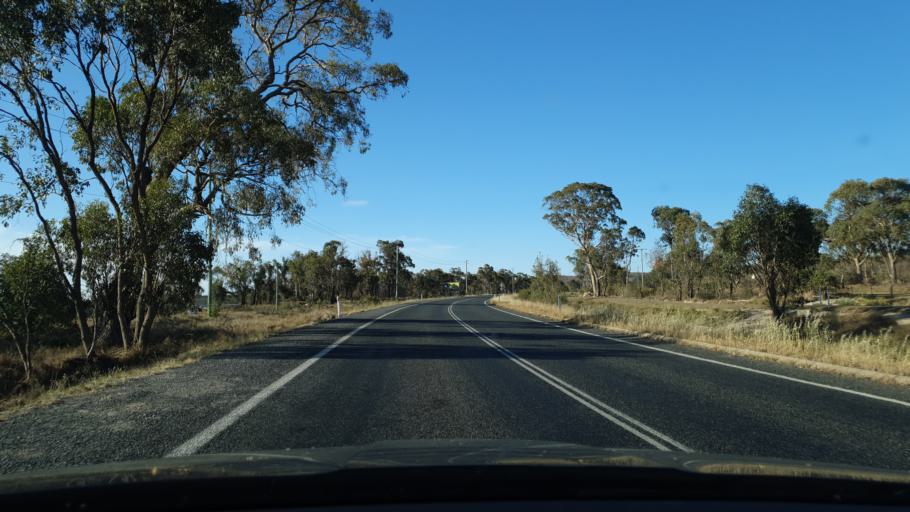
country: AU
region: Queensland
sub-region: Southern Downs
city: Stanthorpe
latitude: -28.6674
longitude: 151.9156
